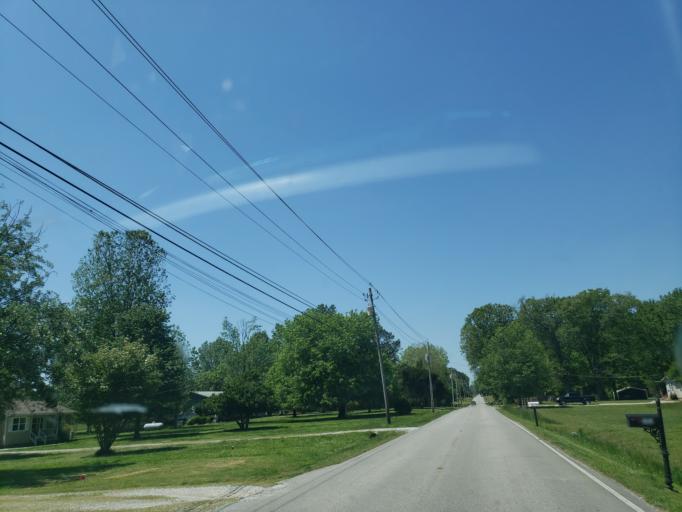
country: US
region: Alabama
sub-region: Madison County
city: Hazel Green
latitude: 34.9624
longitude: -86.6832
